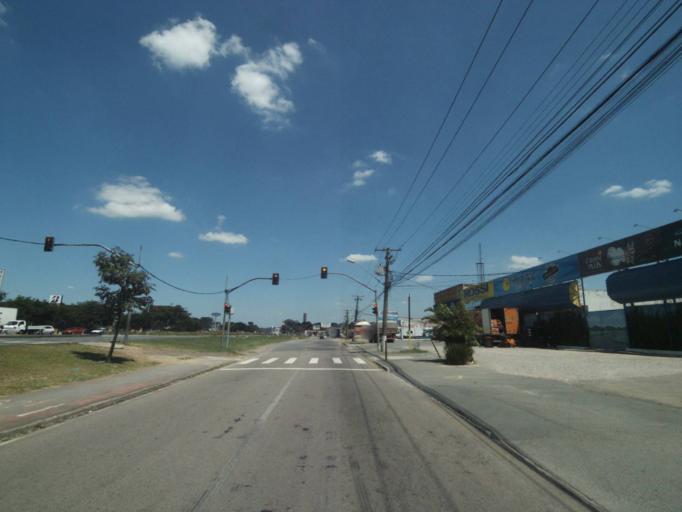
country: BR
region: Parana
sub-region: Sao Jose Dos Pinhais
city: Sao Jose dos Pinhais
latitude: -25.5257
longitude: -49.2975
